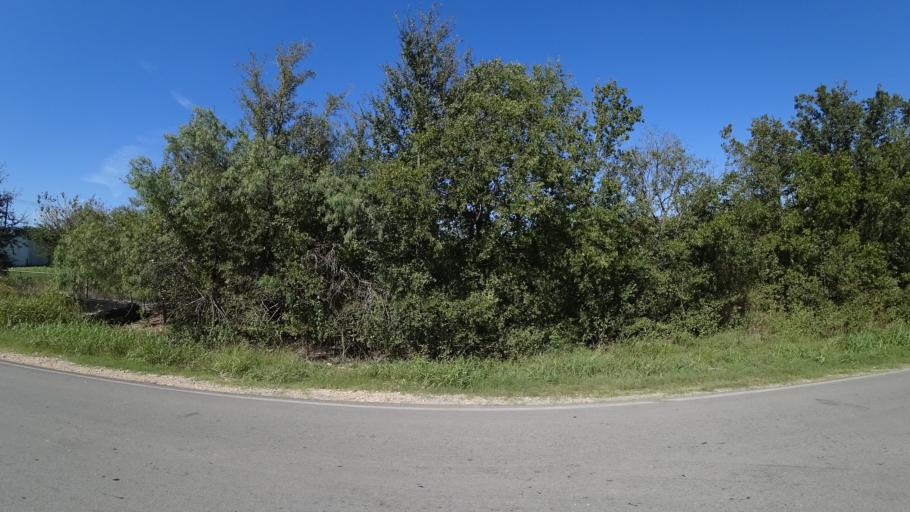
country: US
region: Texas
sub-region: Travis County
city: Hornsby Bend
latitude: 30.2635
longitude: -97.6208
